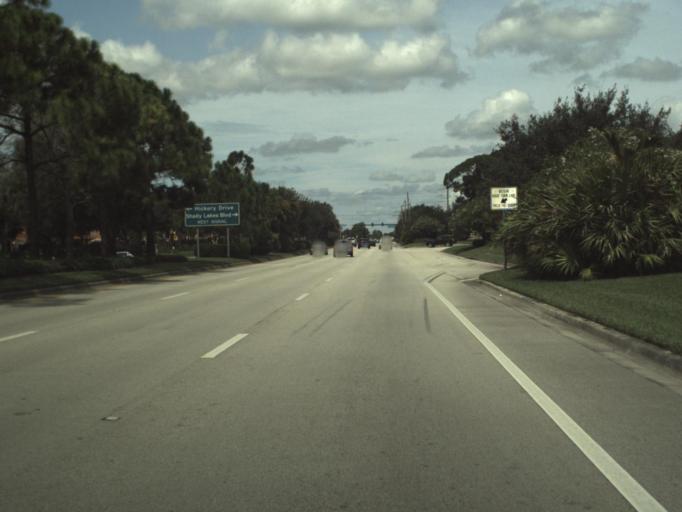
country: US
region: Florida
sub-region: Palm Beach County
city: Palm Beach Gardens
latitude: 26.8385
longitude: -80.1099
